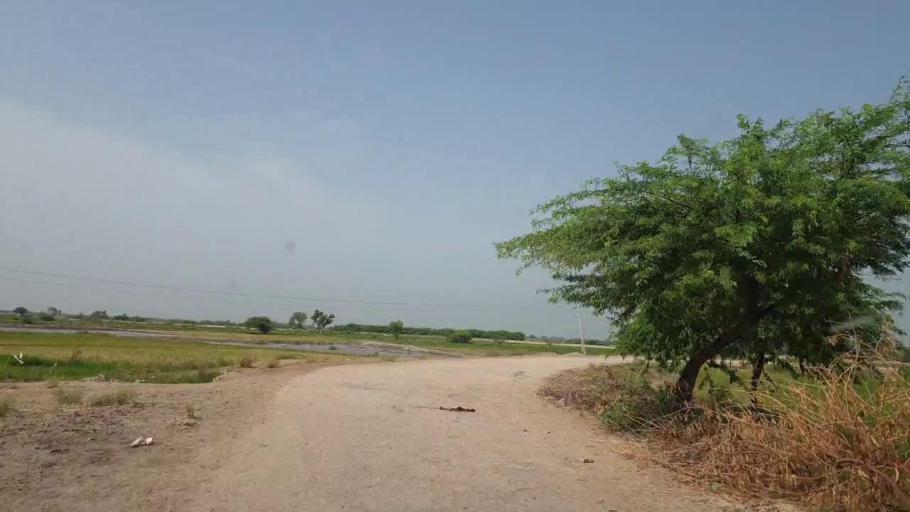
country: PK
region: Sindh
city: Lakhi
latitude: 27.8267
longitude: 68.6911
